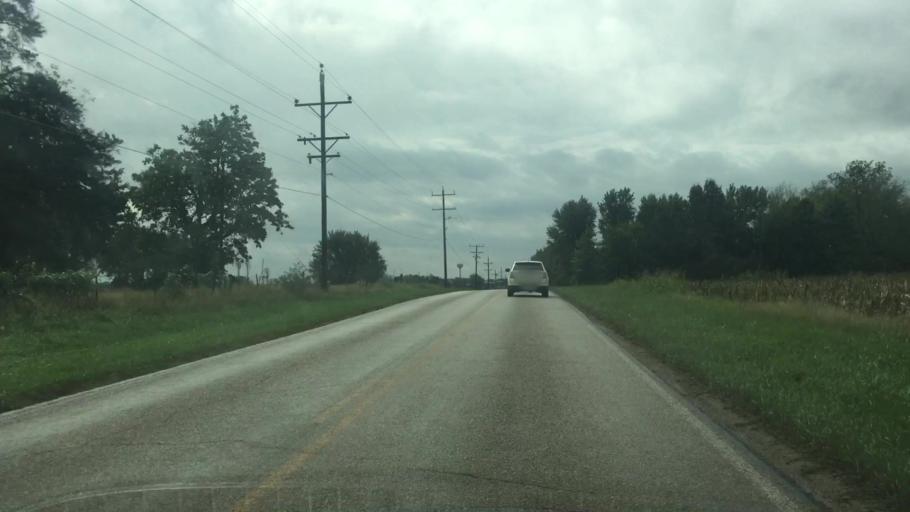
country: US
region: Kansas
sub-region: Allen County
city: Humboldt
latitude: 37.8394
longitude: -95.4368
